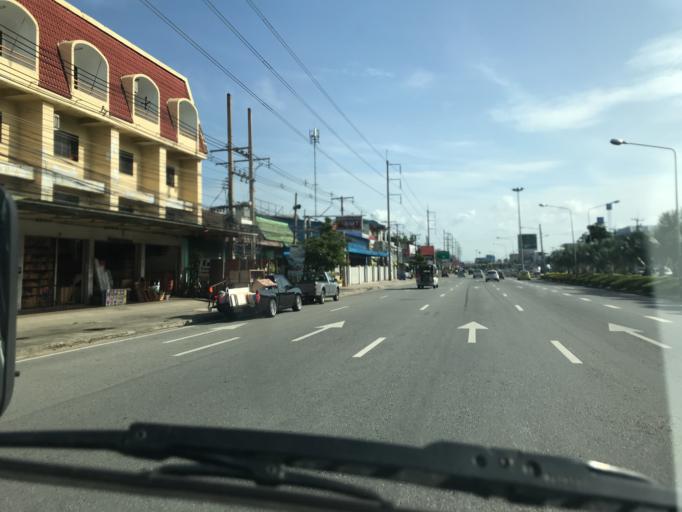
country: TH
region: Chon Buri
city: Bang Lamung
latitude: 13.0137
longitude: 100.9312
